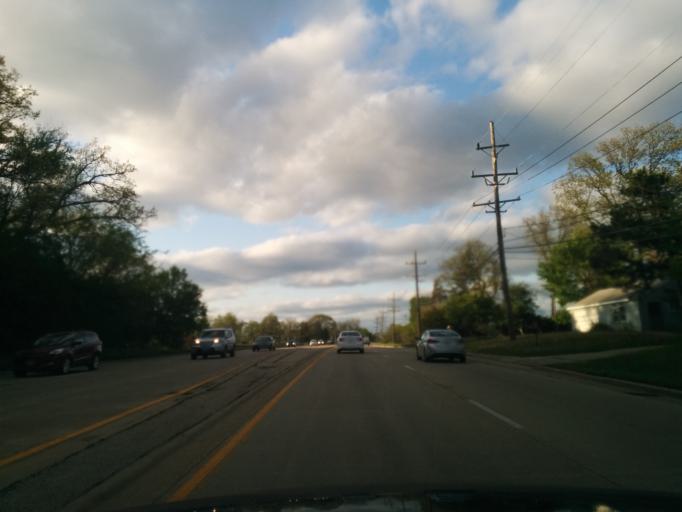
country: US
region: Illinois
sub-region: DuPage County
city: Wayne
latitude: 41.9433
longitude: -88.2084
